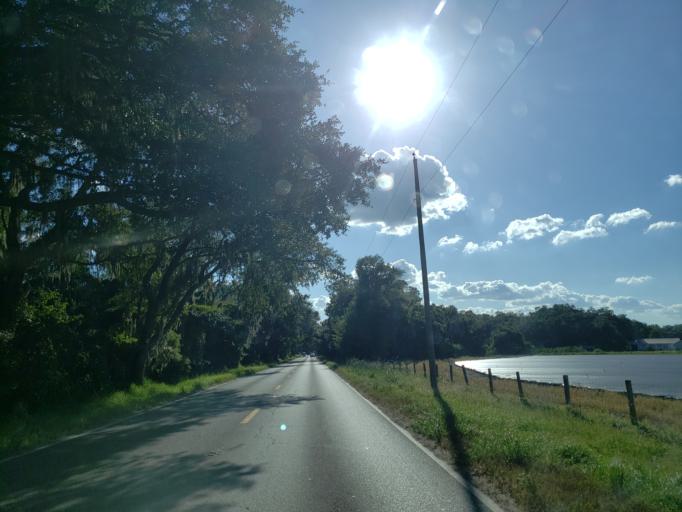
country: US
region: Florida
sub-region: Hillsborough County
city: Dover
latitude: 27.9800
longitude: -82.1810
